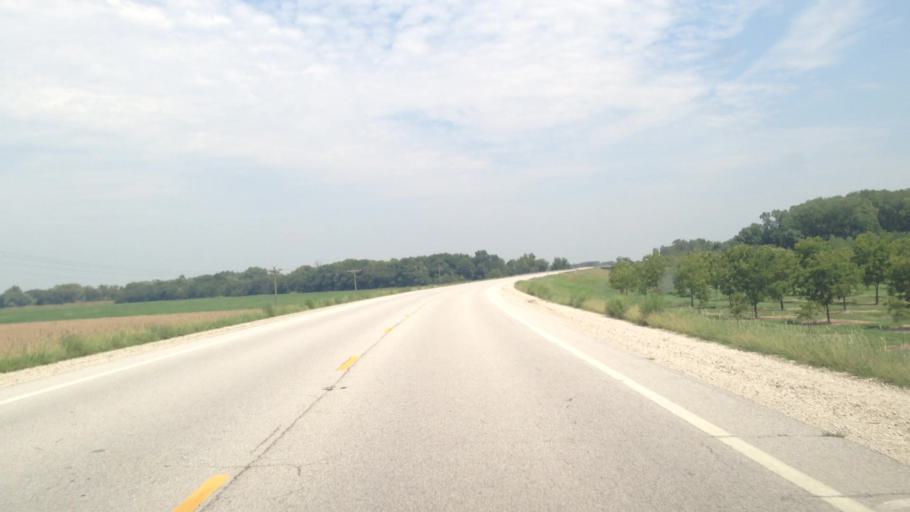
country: US
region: Kansas
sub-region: Neosho County
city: Erie
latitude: 37.5442
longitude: -95.2685
